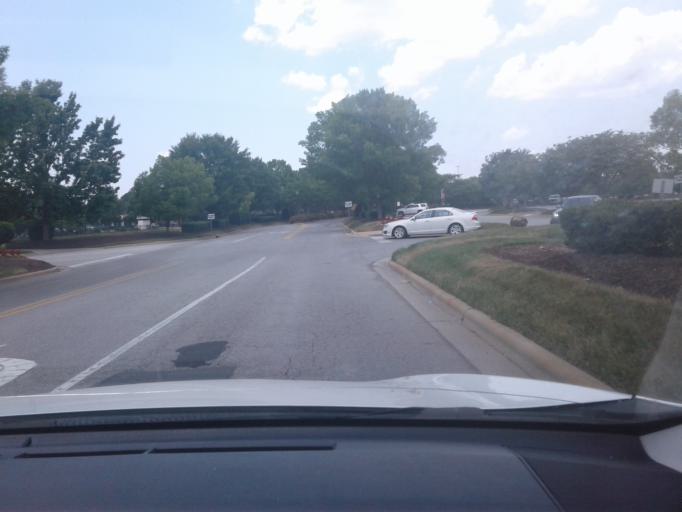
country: US
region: North Carolina
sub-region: Wake County
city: Garner
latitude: 35.6921
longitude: -78.5809
